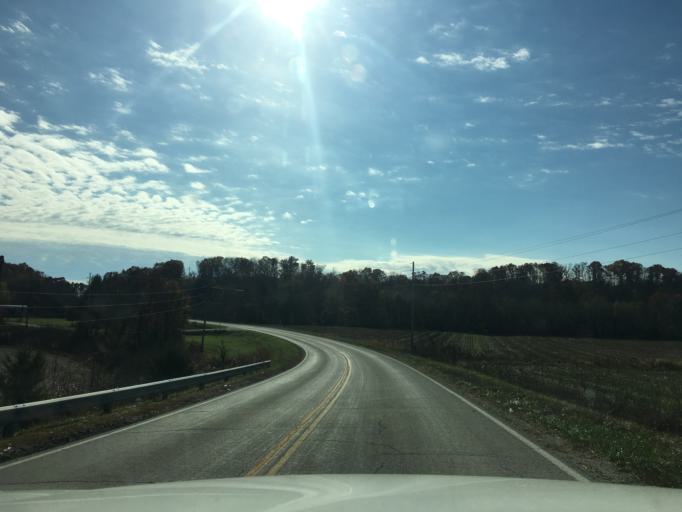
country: US
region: Missouri
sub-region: Osage County
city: Linn
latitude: 38.3965
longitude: -91.8231
